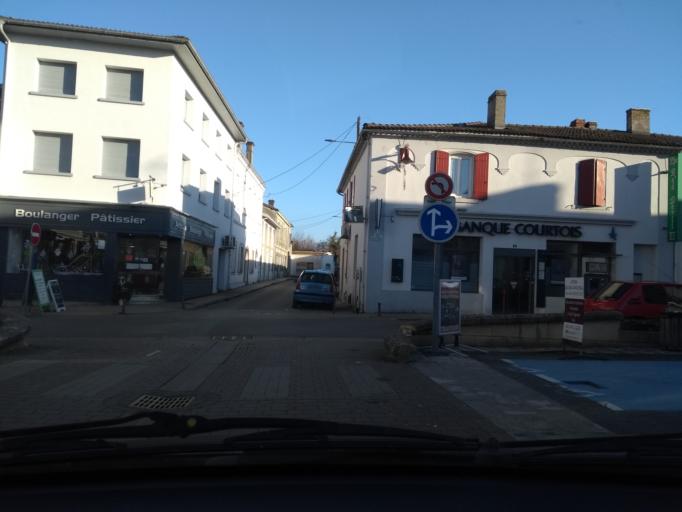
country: FR
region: Aquitaine
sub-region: Departement de la Gironde
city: Salles
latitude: 44.5517
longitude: -0.8701
